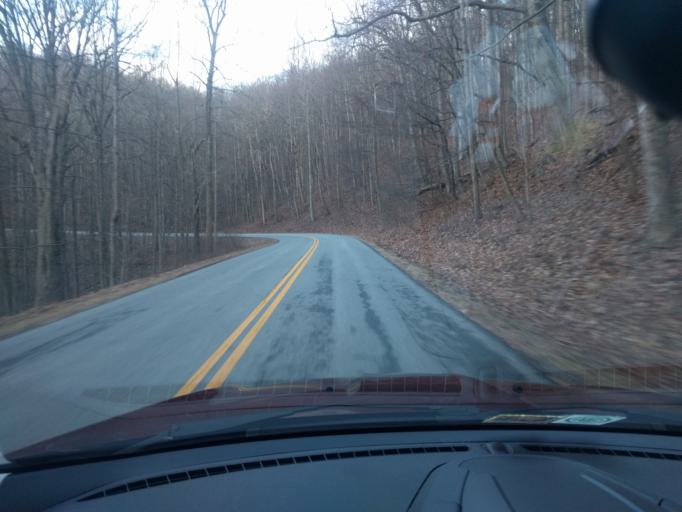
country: US
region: Virginia
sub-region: Botetourt County
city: Buchanan
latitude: 37.4637
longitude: -79.6348
